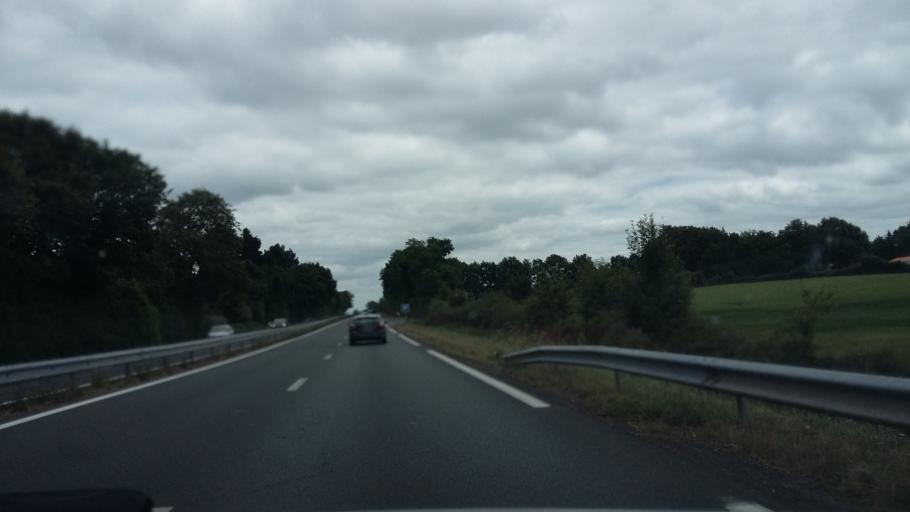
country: FR
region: Pays de la Loire
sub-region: Departement de la Vendee
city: Venansault
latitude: 46.6978
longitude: -1.4881
